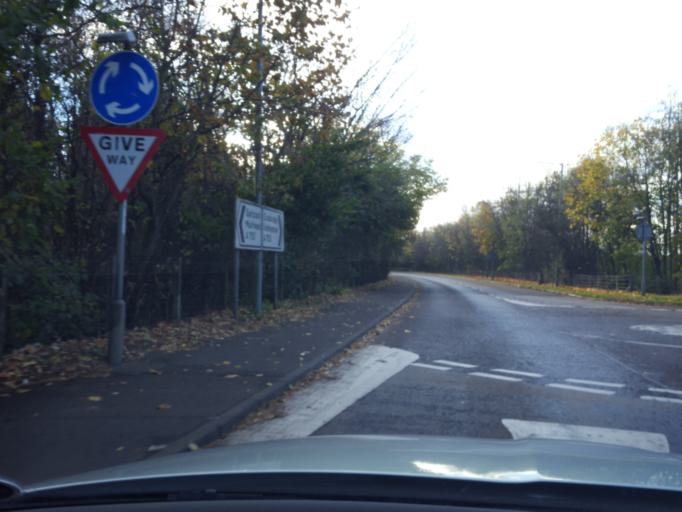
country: GB
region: Scotland
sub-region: North Lanarkshire
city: Chryston
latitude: 55.8859
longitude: -4.0833
